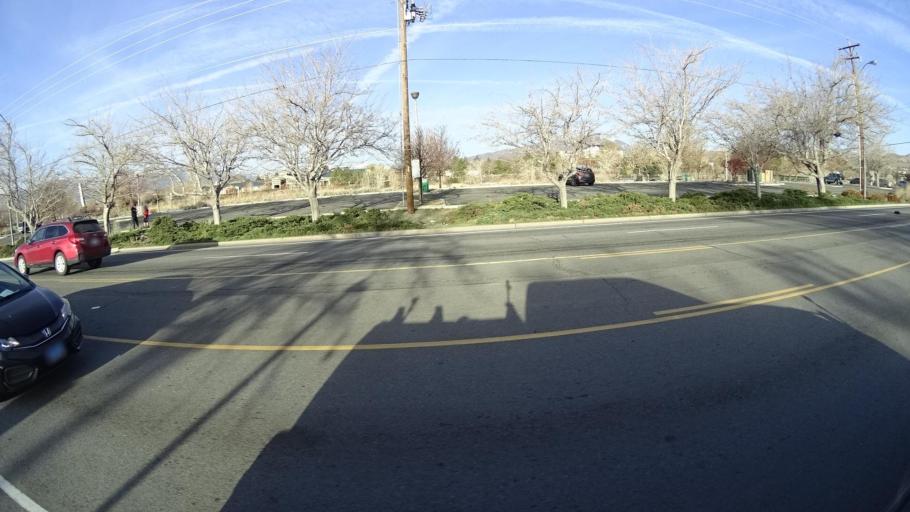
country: US
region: Nevada
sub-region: Washoe County
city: Sparks
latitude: 39.5424
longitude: -119.7760
